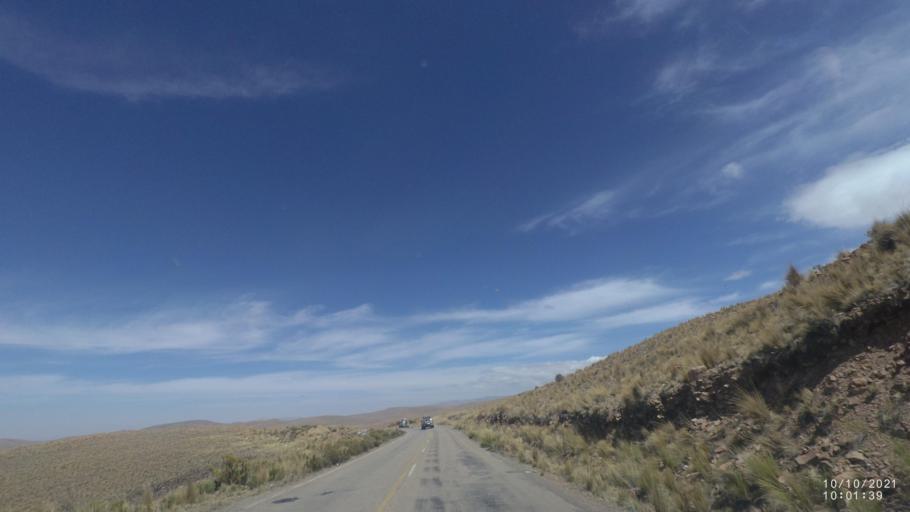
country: BO
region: La Paz
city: Eucaliptus
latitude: -17.3645
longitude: -67.4242
